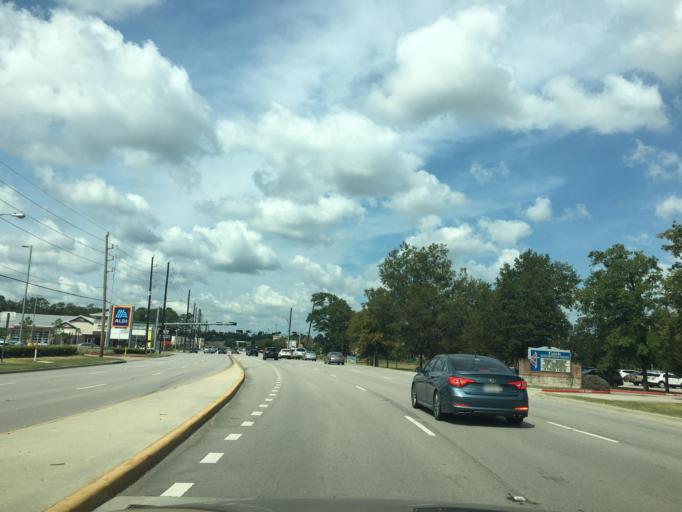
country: US
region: Texas
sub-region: Harris County
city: Spring
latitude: 30.1231
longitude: -95.4040
